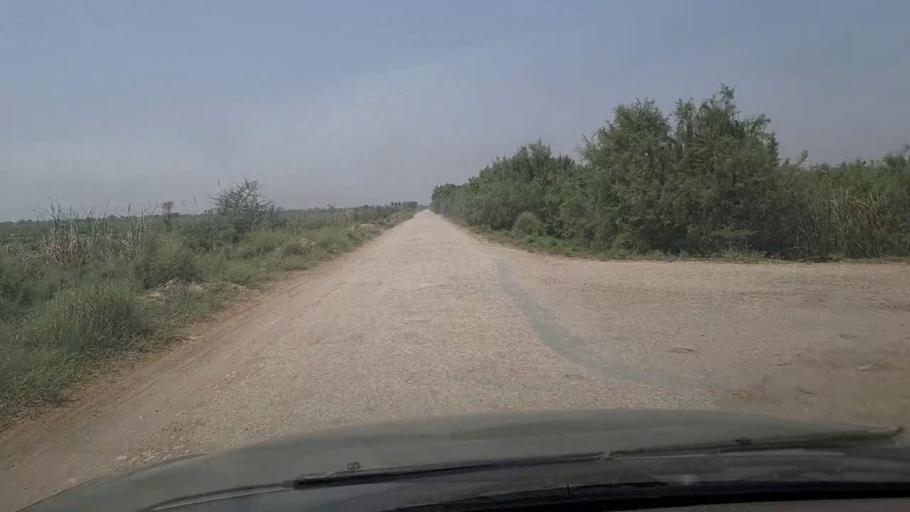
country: PK
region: Sindh
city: Adilpur
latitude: 27.9368
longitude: 69.2874
